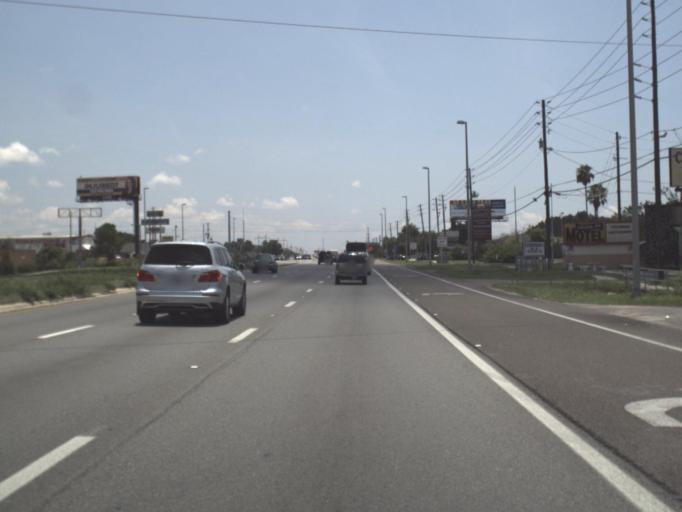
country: US
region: Florida
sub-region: Pasco County
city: Holiday
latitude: 28.1763
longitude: -82.7406
